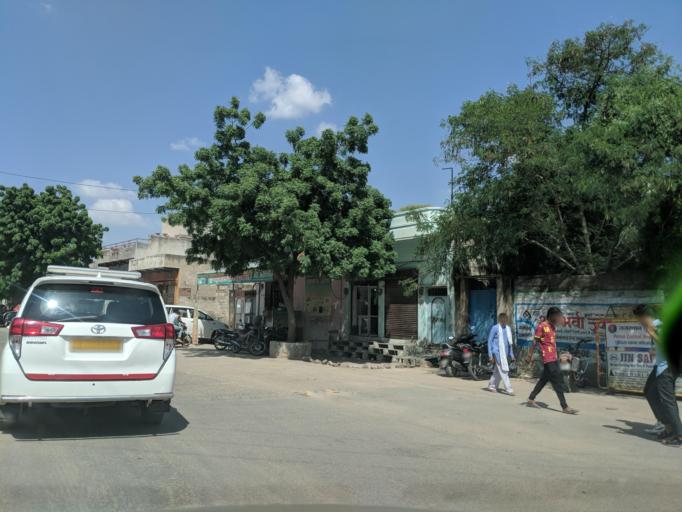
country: IN
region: Rajasthan
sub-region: Jhunjhunun
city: Jhunjhunun
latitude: 28.1347
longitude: 75.3922
